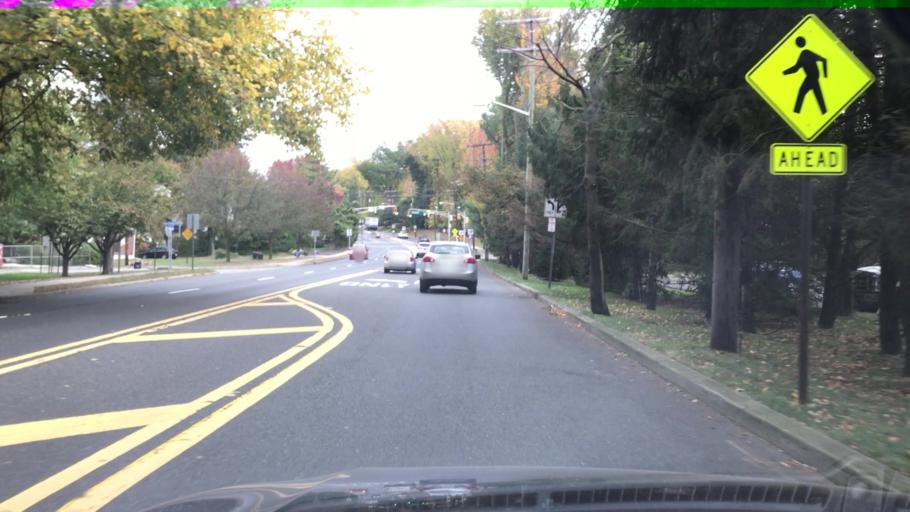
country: US
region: New Jersey
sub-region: Bergen County
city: Teaneck
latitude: 40.9151
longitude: -74.0204
